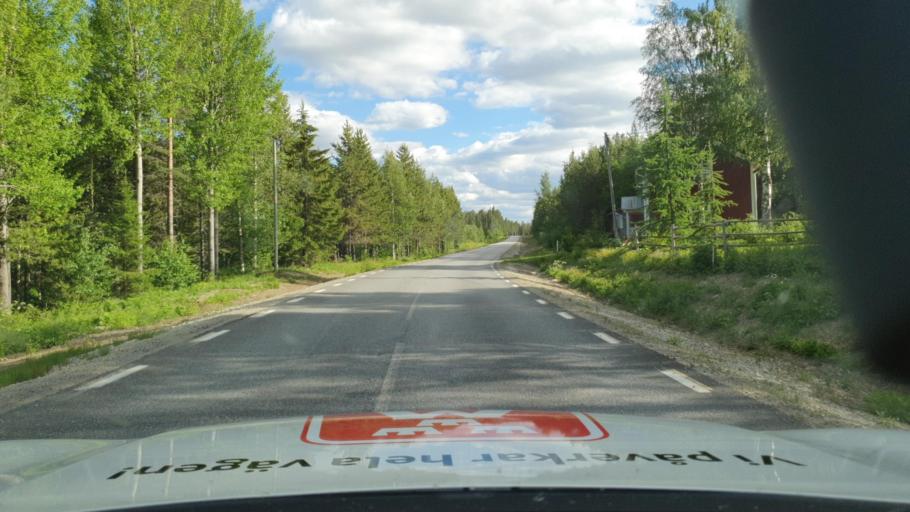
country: SE
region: Vaesterbotten
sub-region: Skelleftea Kommun
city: Langsele
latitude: 64.6872
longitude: 20.0290
